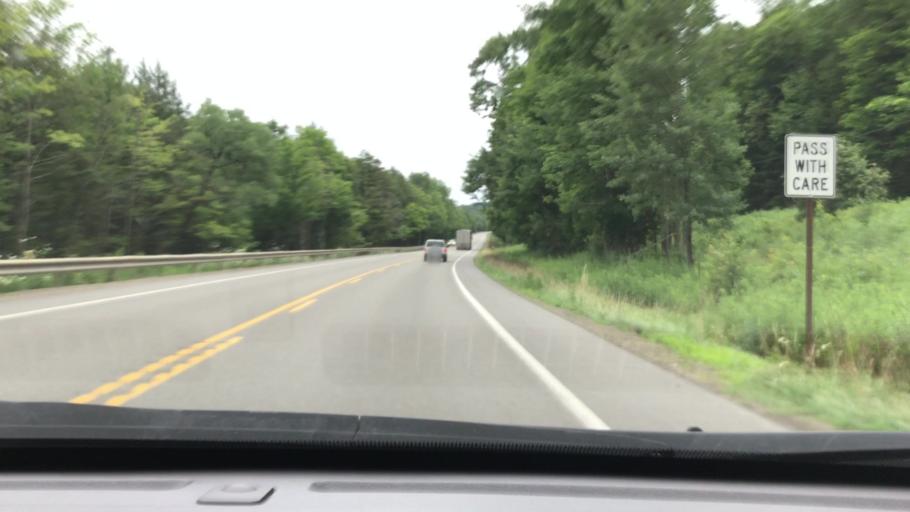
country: US
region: Pennsylvania
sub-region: McKean County
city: Kane
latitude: 41.6774
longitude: -78.6855
